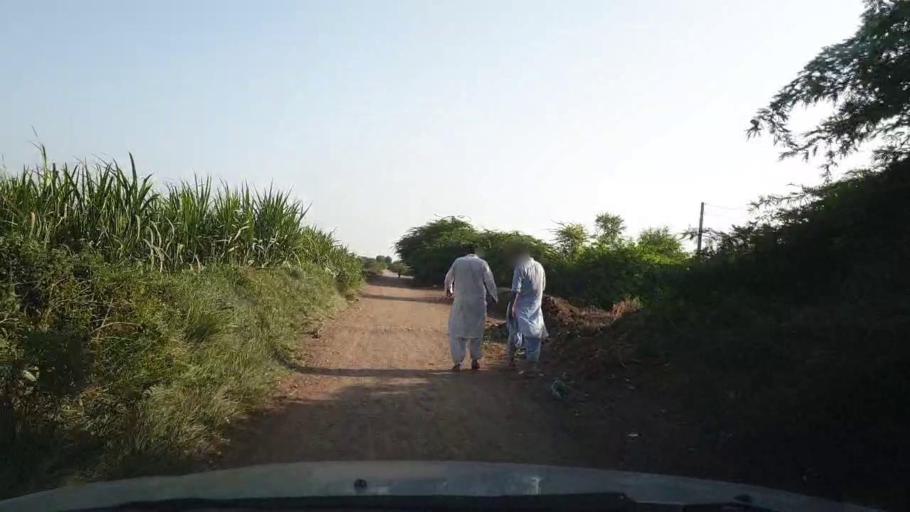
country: PK
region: Sindh
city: Tando Ghulam Ali
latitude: 25.1219
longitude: 68.9407
